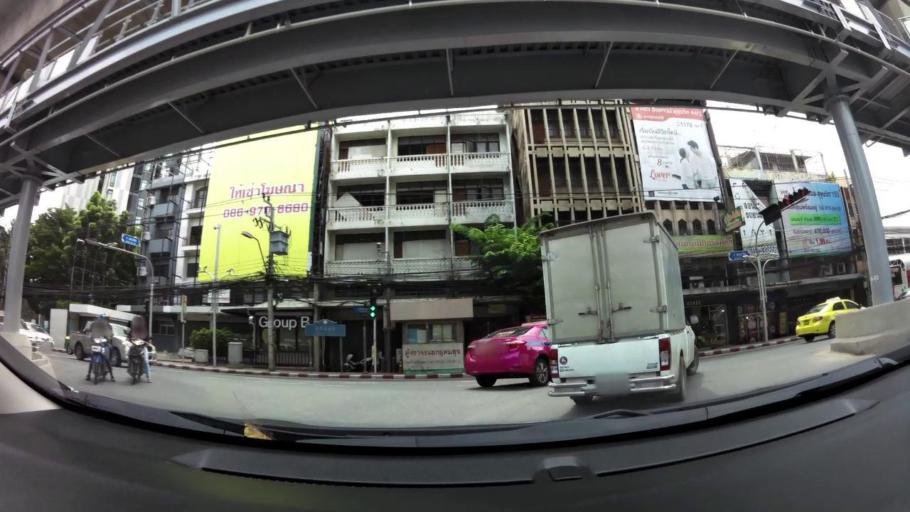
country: TH
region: Bangkok
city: Phra Khanong
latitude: 13.6835
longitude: 100.6102
